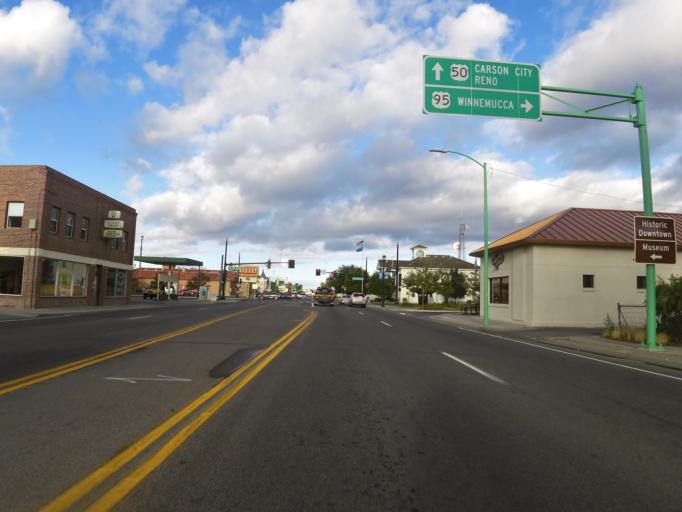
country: US
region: Nevada
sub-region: Churchill County
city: Fallon
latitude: 39.4749
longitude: -118.7760
